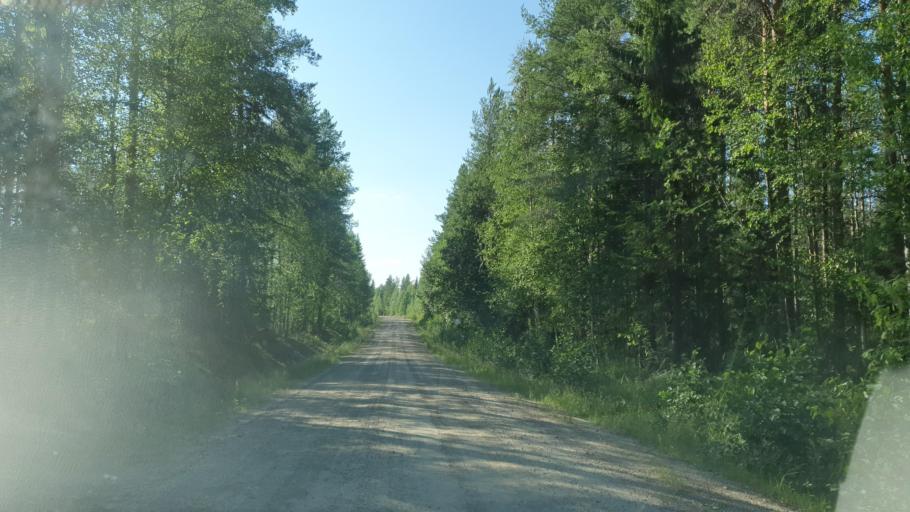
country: FI
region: Kainuu
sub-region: Kehys-Kainuu
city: Kuhmo
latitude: 64.0257
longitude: 29.7186
